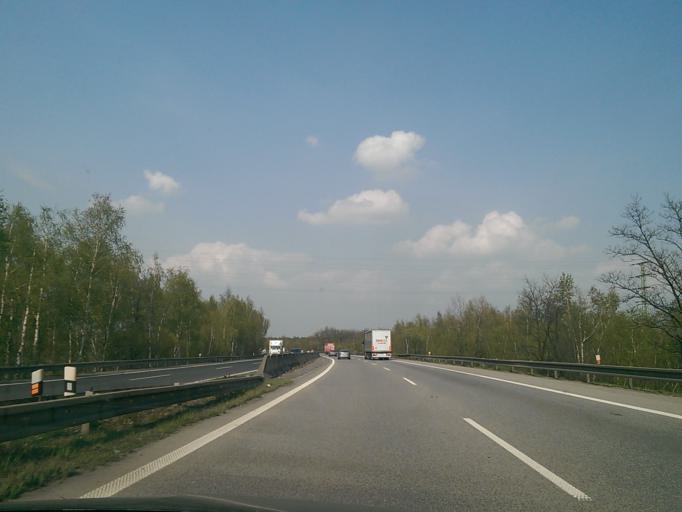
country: CZ
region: Central Bohemia
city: Brandys nad Labem-Stara Boleslav
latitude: 50.1823
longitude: 14.6944
